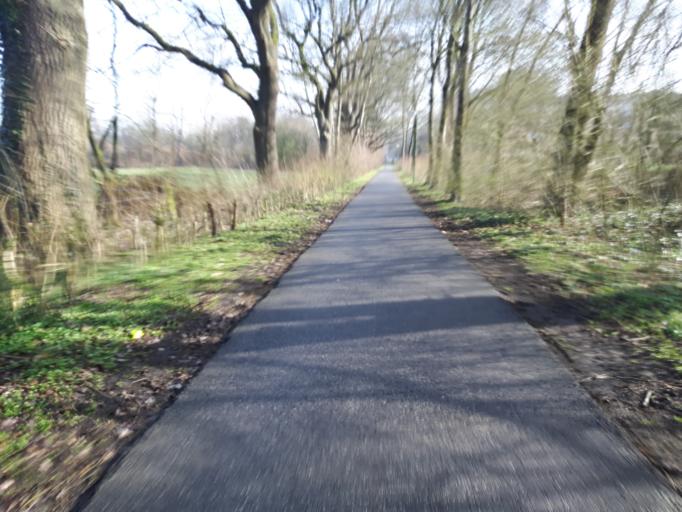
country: DE
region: North Rhine-Westphalia
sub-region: Regierungsbezirk Munster
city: Haltern
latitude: 51.7531
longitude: 7.2027
